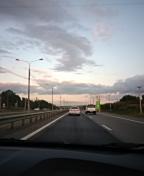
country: RU
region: Moskovskaya
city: Zhukovskiy
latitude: 55.5392
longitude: 38.0902
